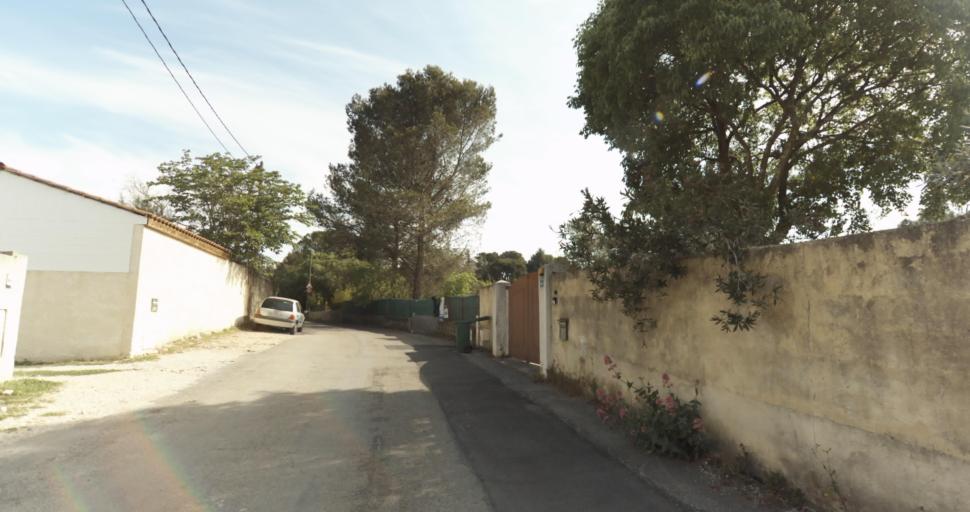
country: FR
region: Languedoc-Roussillon
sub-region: Departement du Gard
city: Nimes
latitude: 43.8605
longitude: 4.3828
